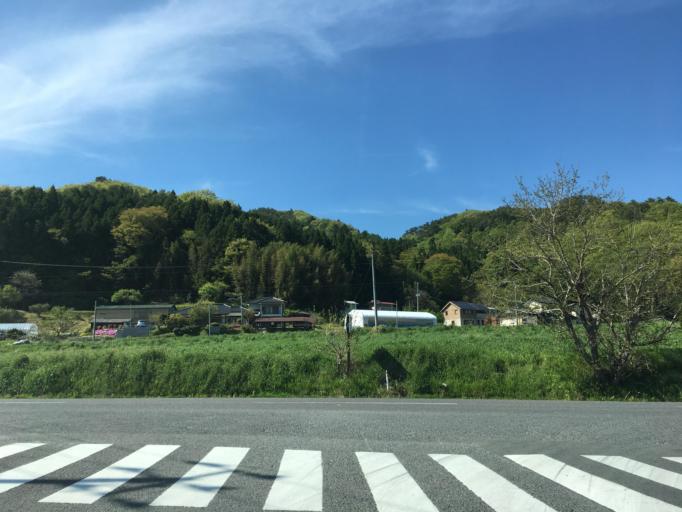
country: JP
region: Fukushima
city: Funehikimachi-funehiki
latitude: 37.3550
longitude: 140.6310
